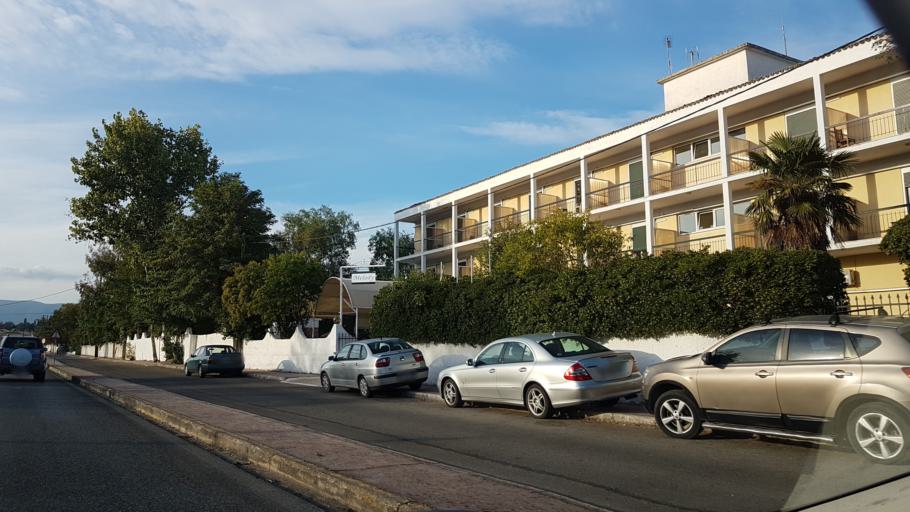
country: GR
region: Ionian Islands
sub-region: Nomos Kerkyras
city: Kontokali
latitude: 39.6503
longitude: 19.8442
